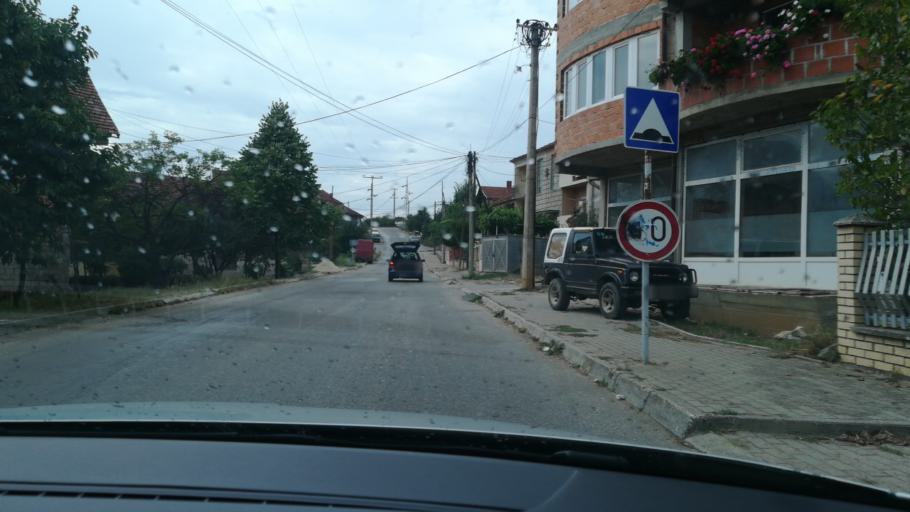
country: MK
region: Kicevo
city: Kicevo
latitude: 41.5105
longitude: 20.9485
